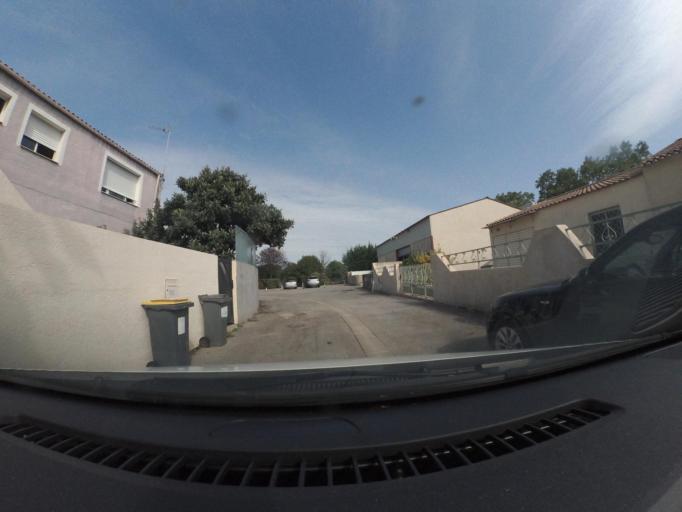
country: FR
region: Languedoc-Roussillon
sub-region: Departement de l'Herault
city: Saint-Bres
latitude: 43.6612
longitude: 4.0256
